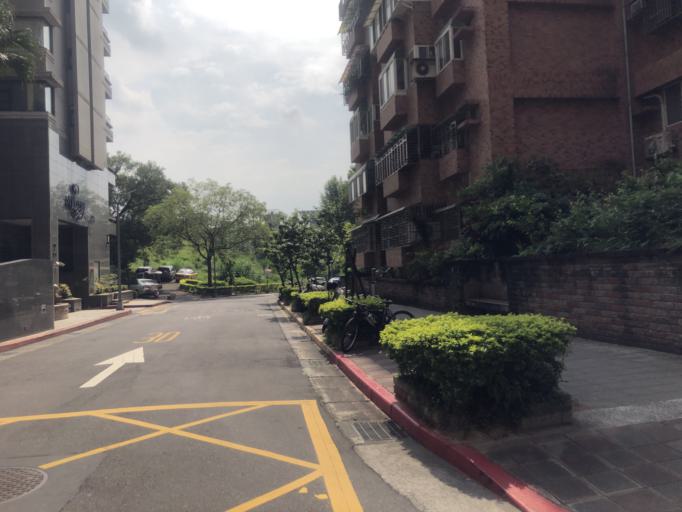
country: TW
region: Taipei
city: Taipei
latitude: 25.0842
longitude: 121.5379
